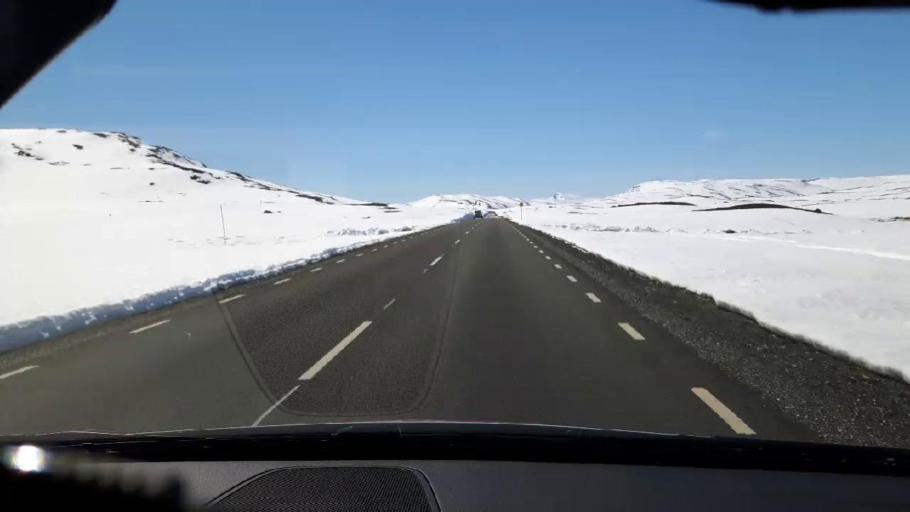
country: NO
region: Nordland
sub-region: Hattfjelldal
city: Hattfjelldal
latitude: 65.0259
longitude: 14.3290
